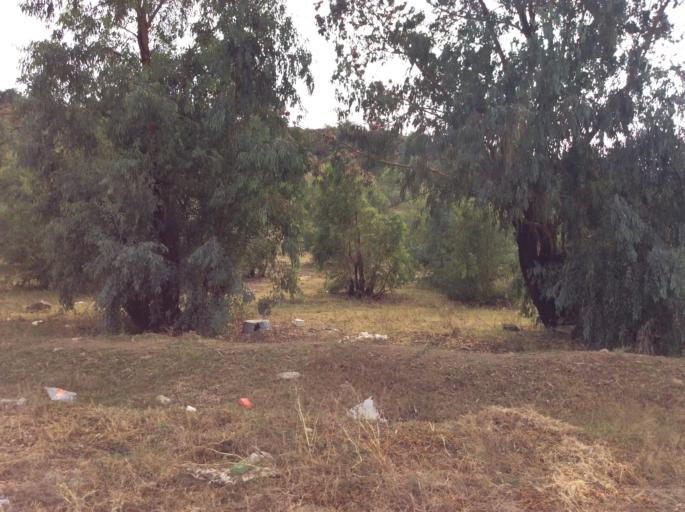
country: LS
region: Mafeteng
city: Mafeteng
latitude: -29.7252
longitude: 27.0337
